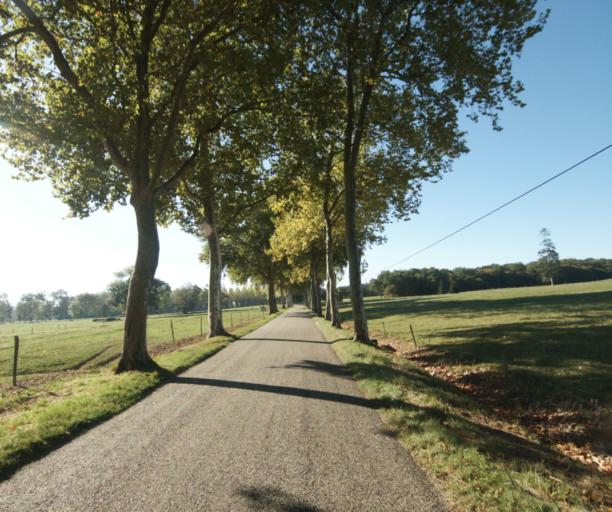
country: FR
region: Midi-Pyrenees
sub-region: Departement du Gers
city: Vic-Fezensac
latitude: 43.8351
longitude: 0.2876
